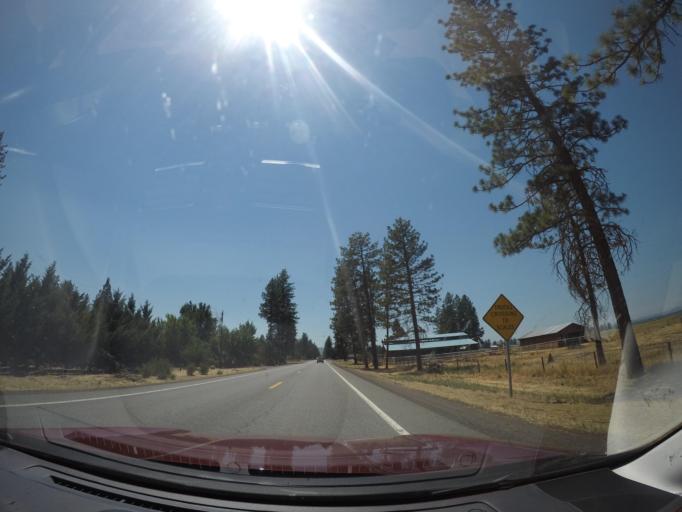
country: US
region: California
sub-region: Shasta County
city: Burney
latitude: 41.0662
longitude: -121.3528
